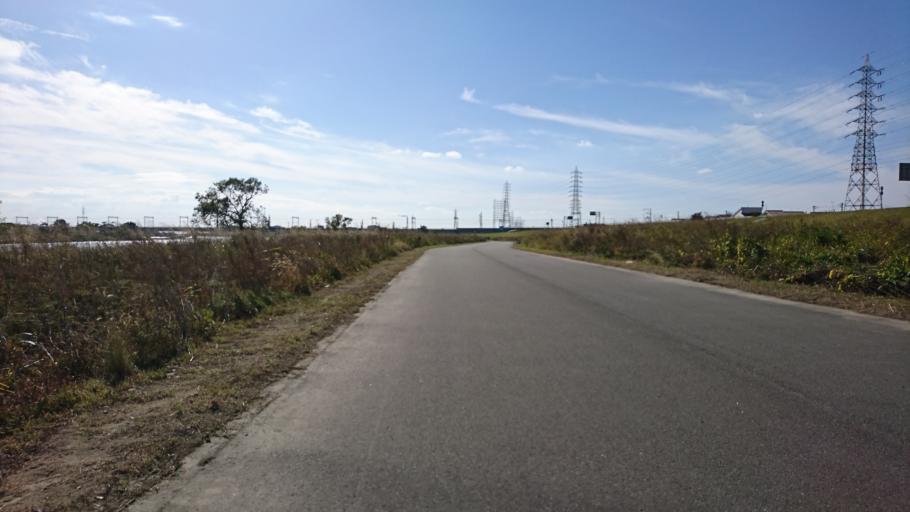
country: JP
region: Hyogo
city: Kakogawacho-honmachi
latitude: 34.7661
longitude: 134.8082
